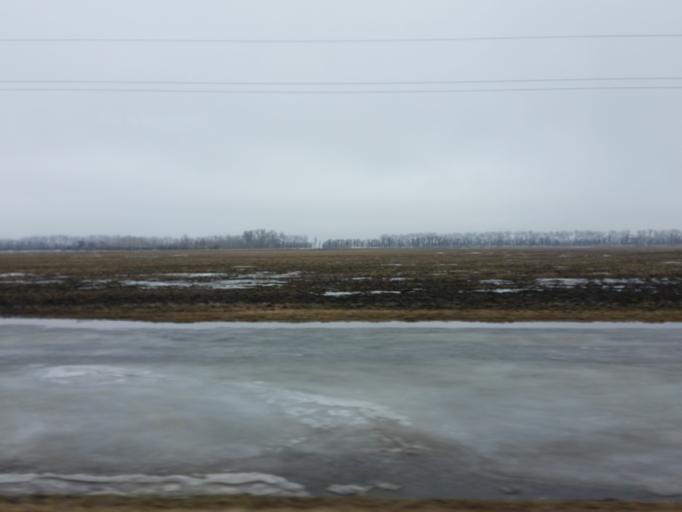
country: US
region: North Dakota
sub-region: Walsh County
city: Grafton
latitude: 48.5720
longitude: -97.4236
